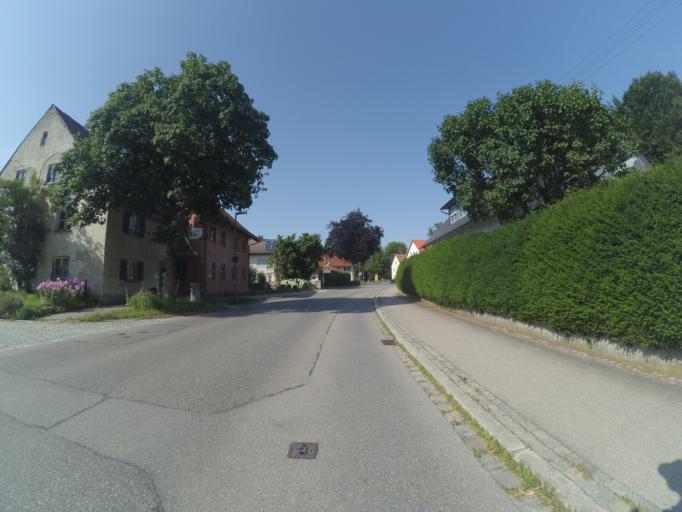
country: DE
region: Bavaria
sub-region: Swabia
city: Buchloe
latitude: 48.0402
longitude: 10.7299
